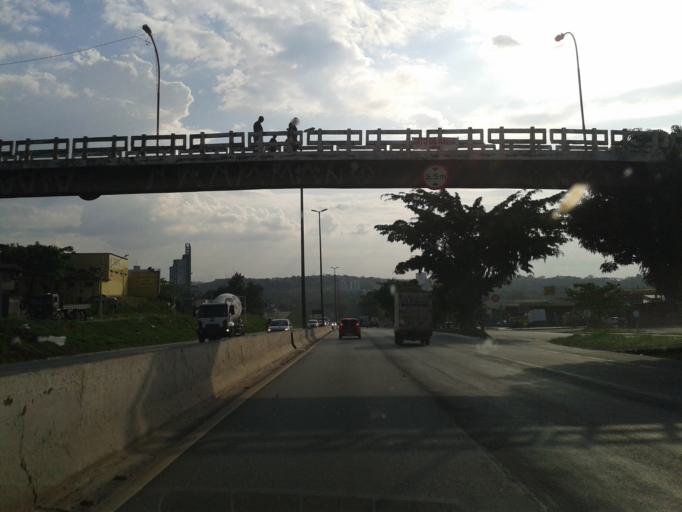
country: BR
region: Minas Gerais
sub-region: Belo Horizonte
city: Belo Horizonte
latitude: -19.8820
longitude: -43.9586
